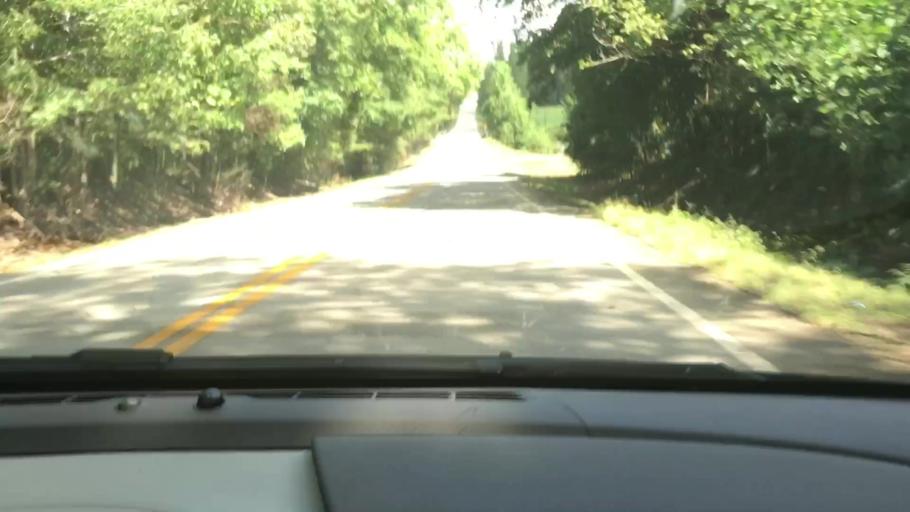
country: US
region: Georgia
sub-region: Troup County
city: La Grange
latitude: 32.9248
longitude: -85.0201
